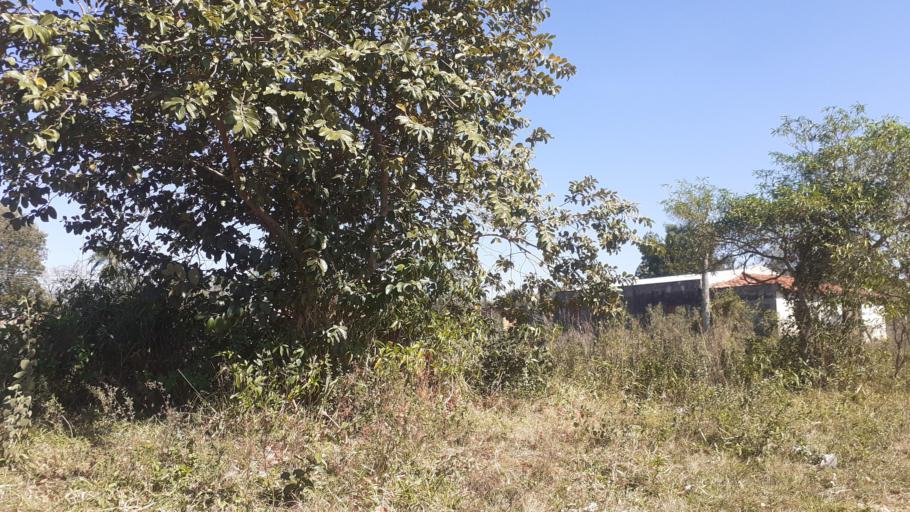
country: PY
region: Misiones
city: San Juan Bautista
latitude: -26.6662
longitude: -57.1262
